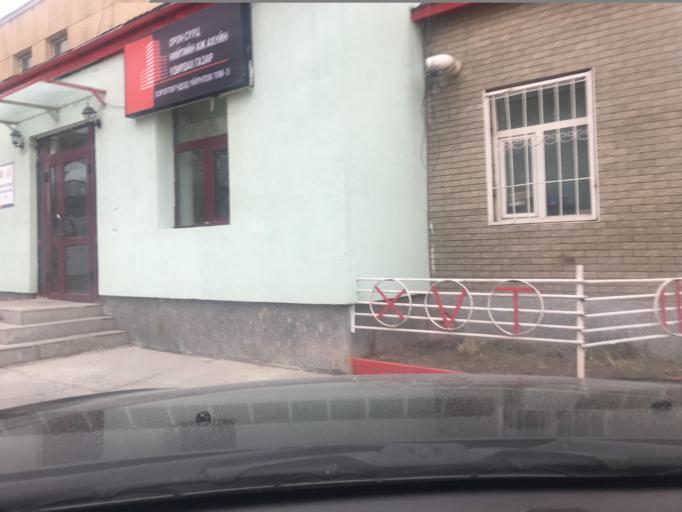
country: MN
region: Ulaanbaatar
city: Ulaanbaatar
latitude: 47.9231
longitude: 106.9391
